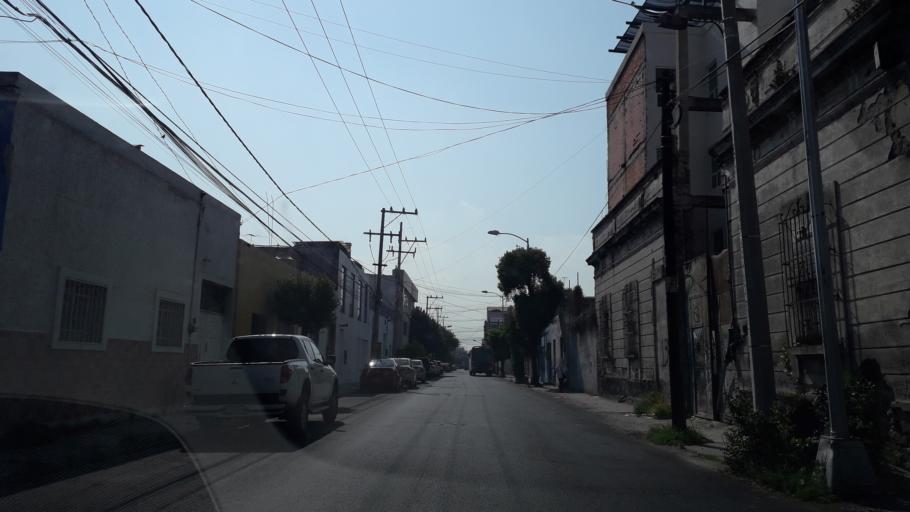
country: MX
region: Puebla
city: Puebla
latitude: 19.0417
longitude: -98.2126
